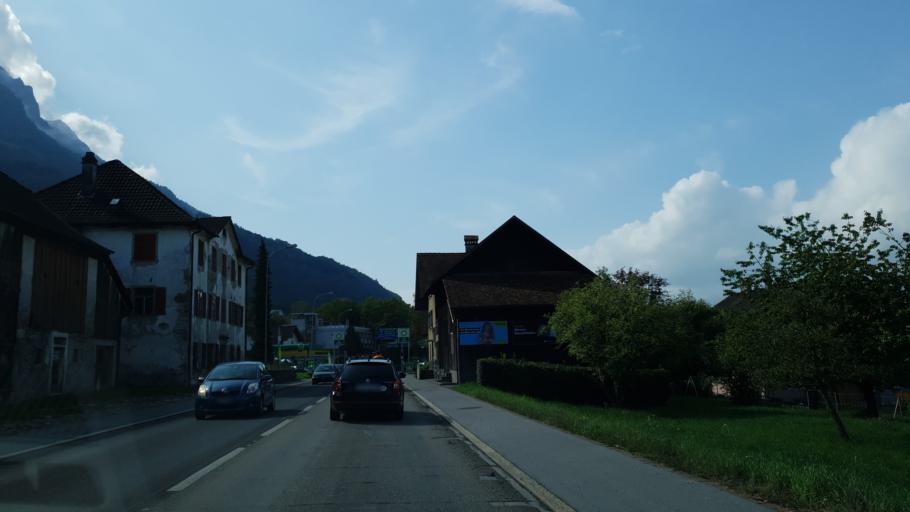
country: LI
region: Mauren
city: Mauren
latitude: 47.2019
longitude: 9.5455
